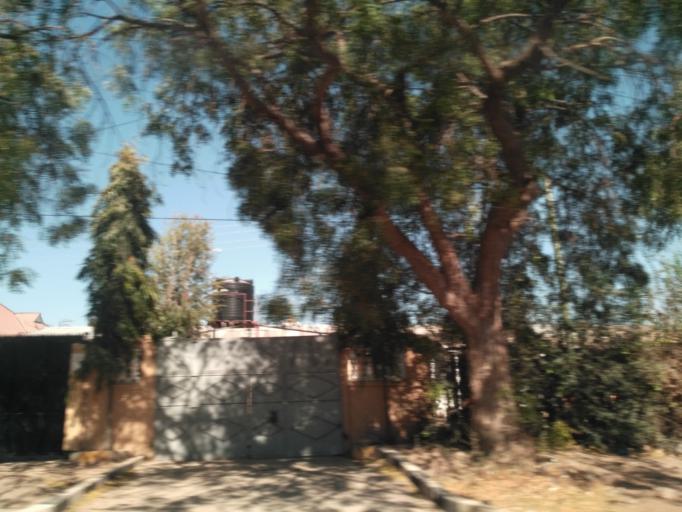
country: TZ
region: Dodoma
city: Dodoma
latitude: -6.1632
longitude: 35.7491
